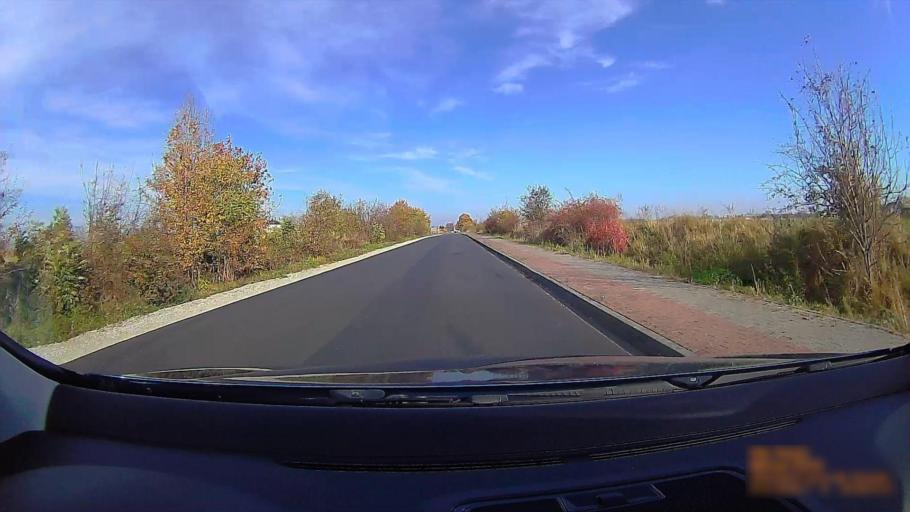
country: PL
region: Greater Poland Voivodeship
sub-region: Powiat ostrzeszowski
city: Doruchow
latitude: 51.4060
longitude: 18.0701
